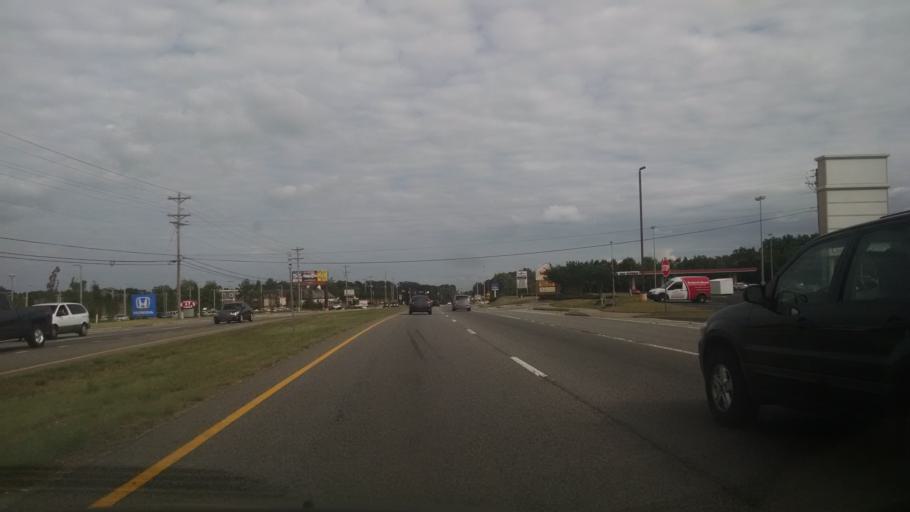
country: US
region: Georgia
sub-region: Forsyth County
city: Cumming
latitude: 34.1761
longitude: -84.1294
